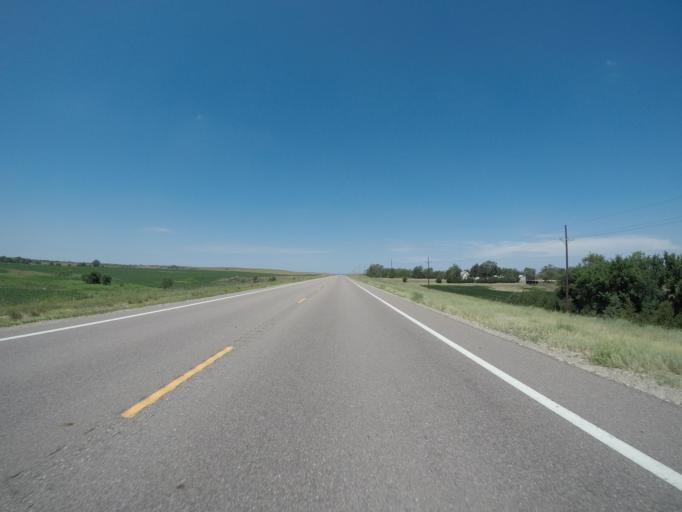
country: US
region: Kansas
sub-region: Osborne County
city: Osborne
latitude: 39.5098
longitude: -98.6607
